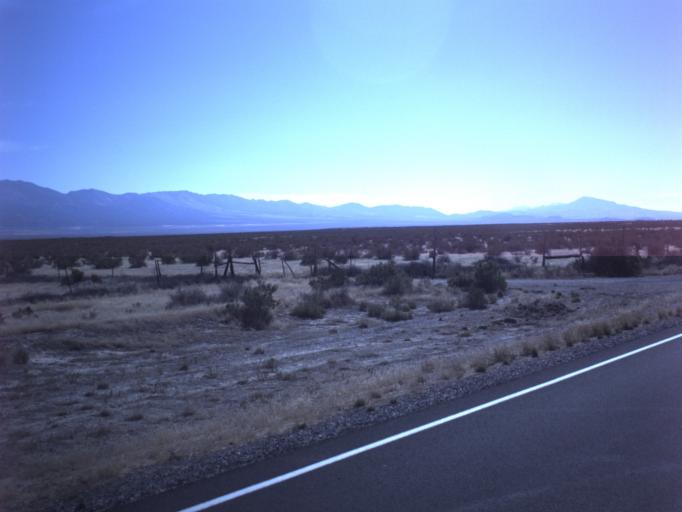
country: US
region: Utah
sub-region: Tooele County
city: Grantsville
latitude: 40.3319
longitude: -112.7444
